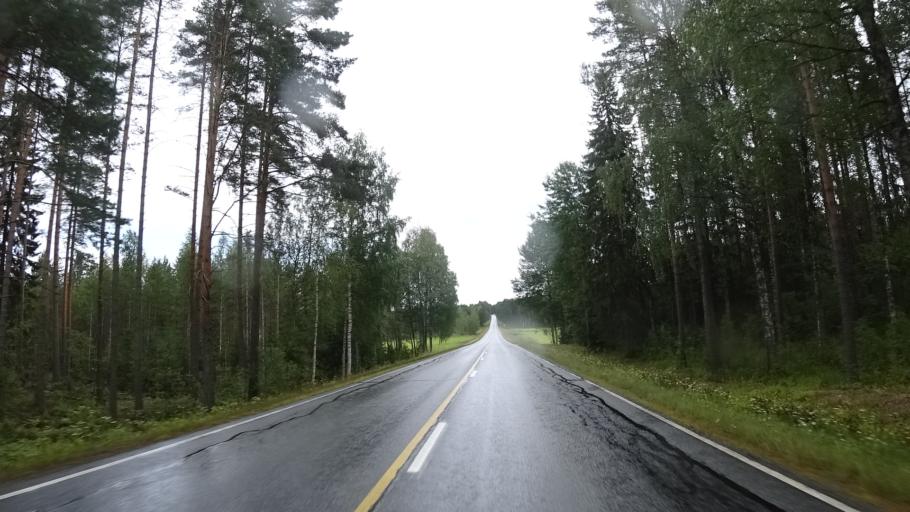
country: FI
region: North Karelia
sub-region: Keski-Karjala
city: Raeaekkylae
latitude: 62.0723
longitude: 29.6283
